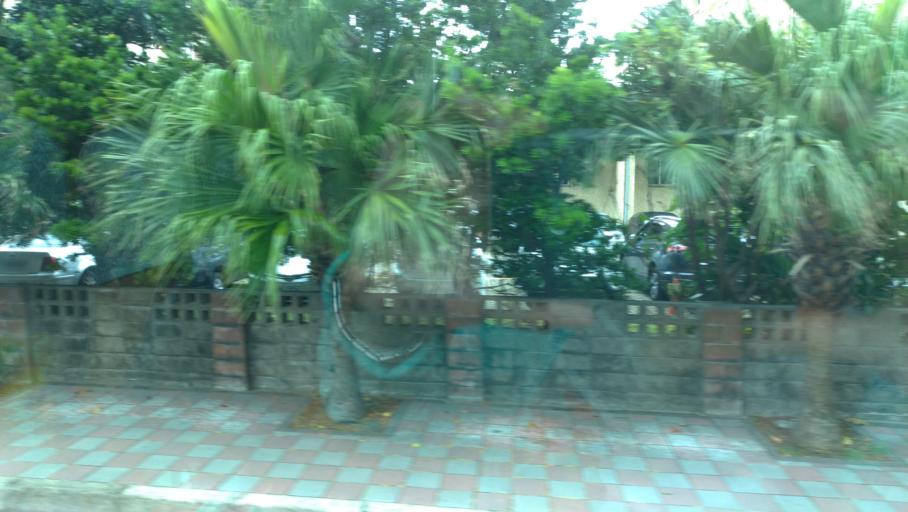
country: TW
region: Taiwan
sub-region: Keelung
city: Keelung
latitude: 25.1500
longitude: 121.7811
